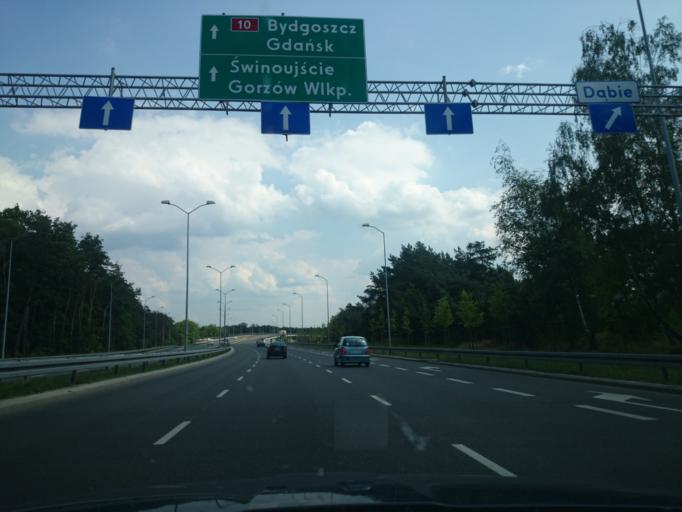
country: PL
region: West Pomeranian Voivodeship
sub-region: Szczecin
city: Szczecin
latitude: 53.3820
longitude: 14.6763
